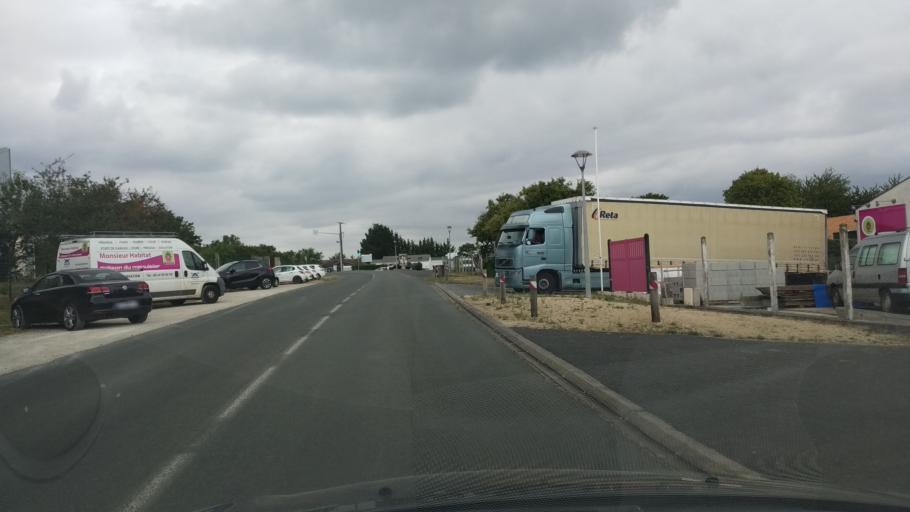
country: FR
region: Poitou-Charentes
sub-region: Departement de la Vienne
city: Smarves
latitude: 46.5056
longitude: 0.3605
